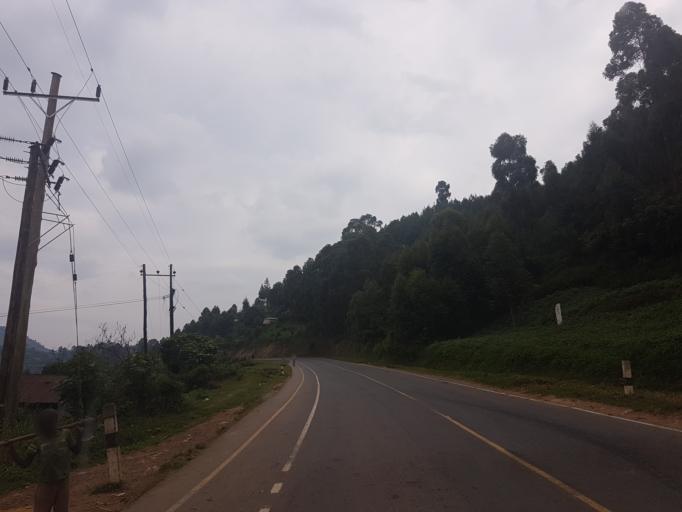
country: UG
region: Western Region
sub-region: Kisoro District
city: Kisoro
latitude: -1.2085
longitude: 29.8223
